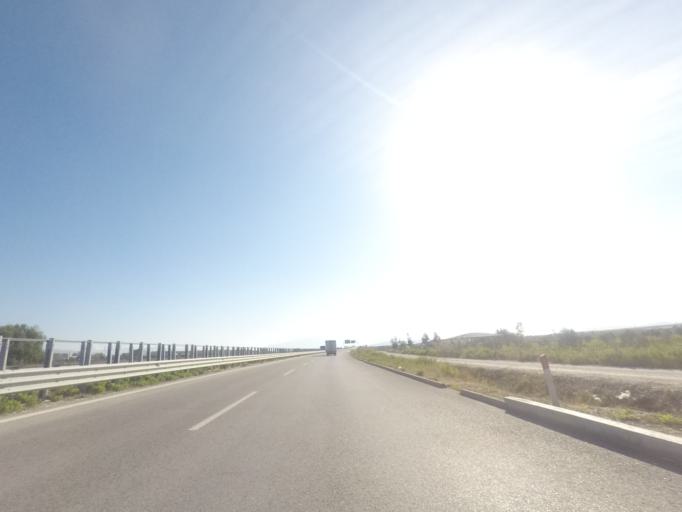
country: AL
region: Vlore
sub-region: Rrethi i Vlores
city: Novosele
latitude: 40.5634
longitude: 19.4676
